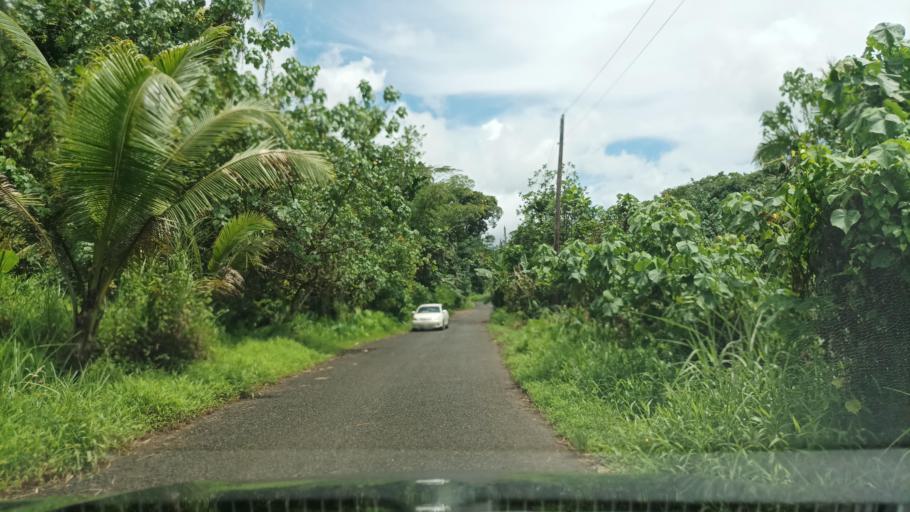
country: FM
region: Pohnpei
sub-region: Kolonia Municipality
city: Kolonia
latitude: 6.9683
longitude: 158.2241
